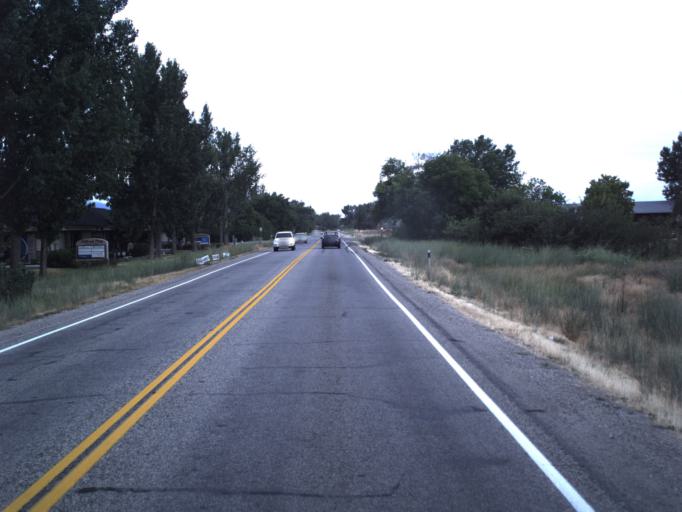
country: US
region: Utah
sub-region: Weber County
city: Marriott-Slaterville
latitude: 41.2651
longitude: -112.0270
